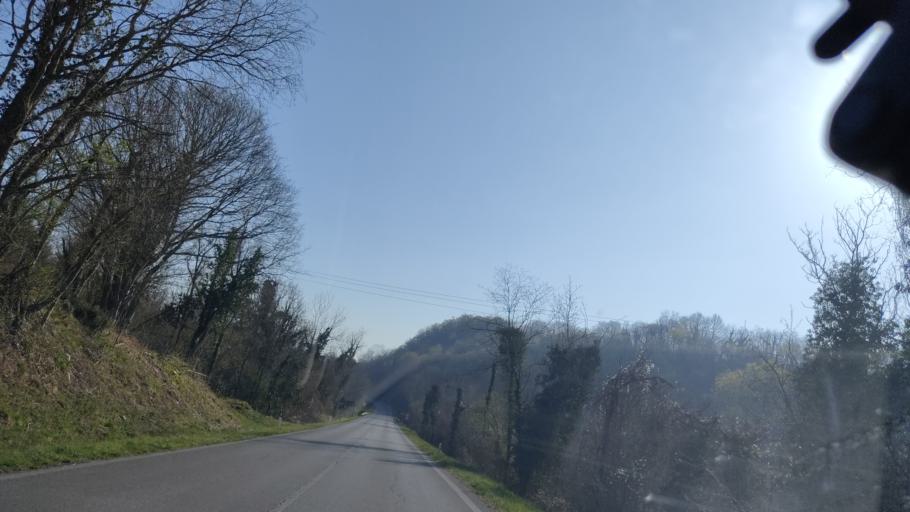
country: IT
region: Friuli Venezia Giulia
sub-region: Provincia di Pordenone
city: Polcenigo
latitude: 46.0411
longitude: 12.5115
